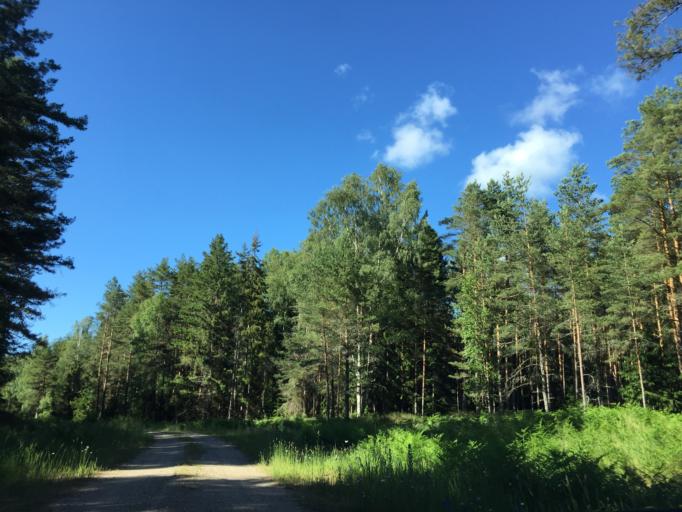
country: LV
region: Ventspils
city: Ventspils
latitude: 57.5474
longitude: 21.7663
